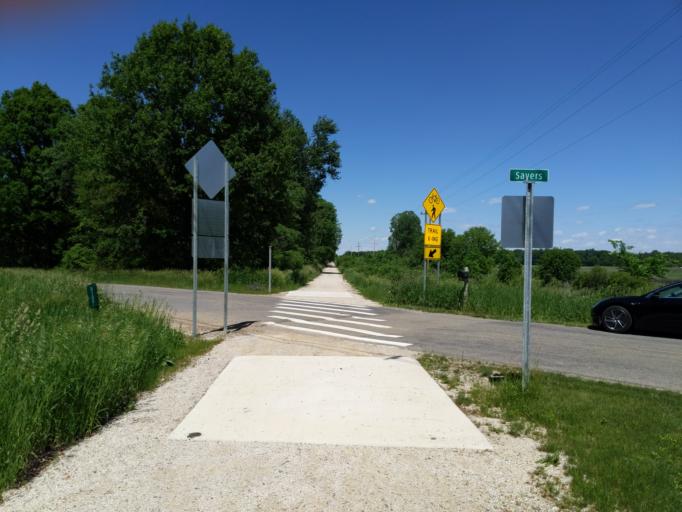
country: US
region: Michigan
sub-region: Ingham County
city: Stockbridge
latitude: 42.3680
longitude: -84.2801
